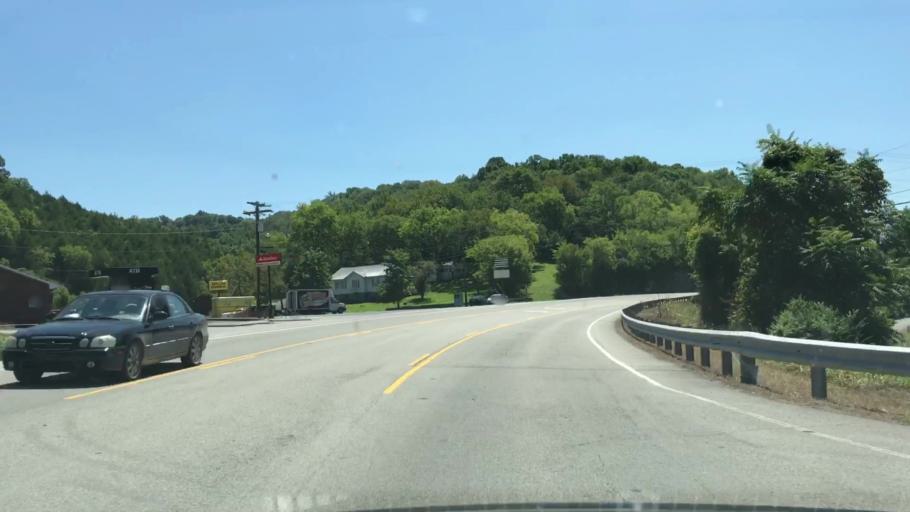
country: US
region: Tennessee
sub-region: Jackson County
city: Gainesboro
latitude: 36.3609
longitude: -85.6541
